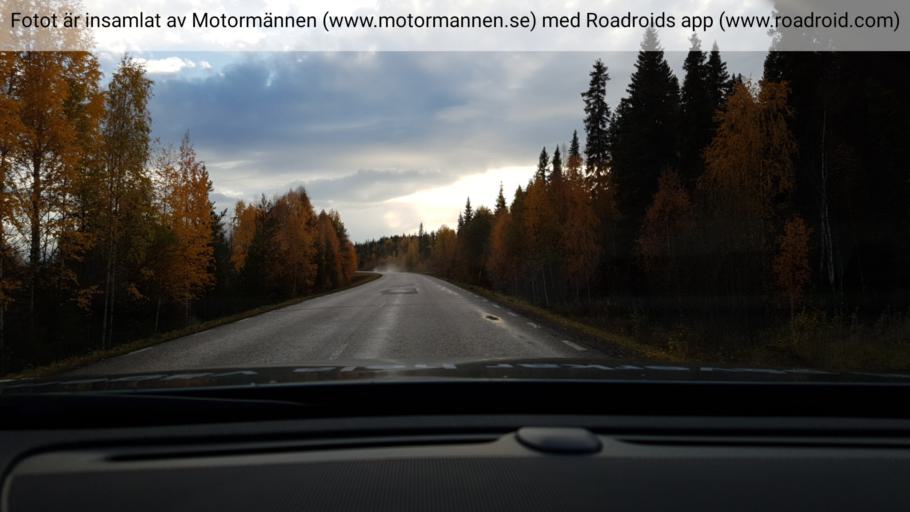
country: SE
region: Norrbotten
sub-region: Overkalix Kommun
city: OEverkalix
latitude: 66.7832
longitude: 22.7096
